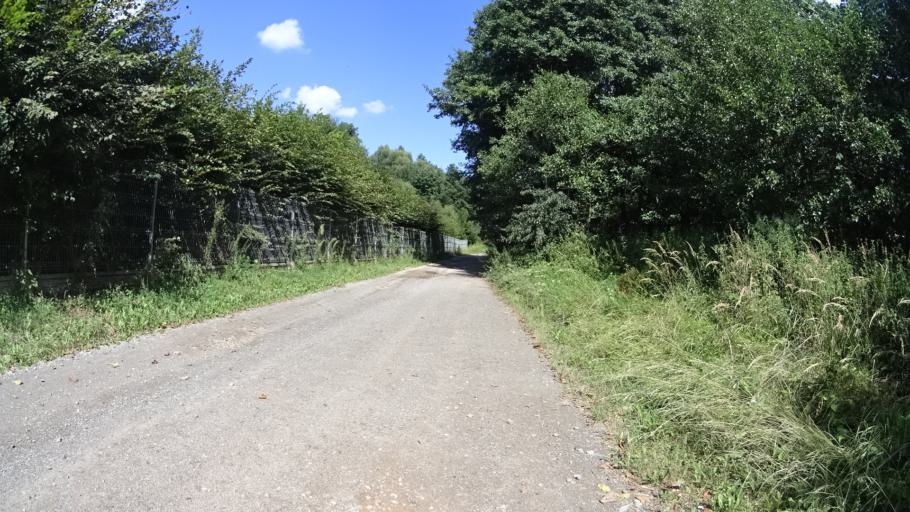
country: PL
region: Masovian Voivodeship
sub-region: Powiat grojecki
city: Mogielnica
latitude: 51.6707
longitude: 20.7452
